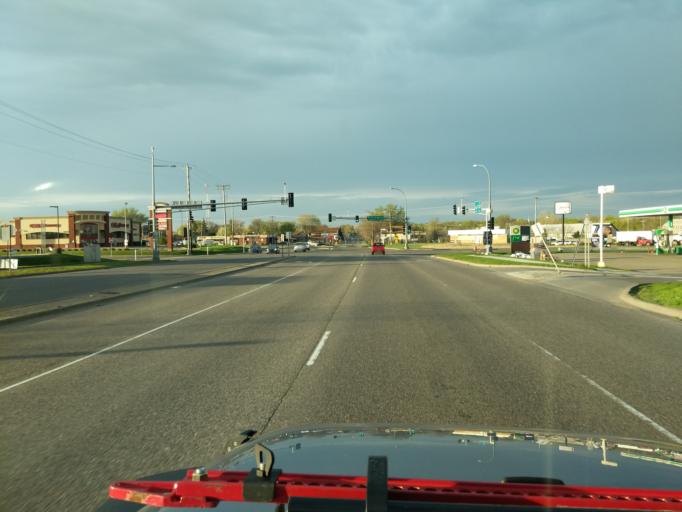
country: US
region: Minnesota
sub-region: Hennepin County
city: Rogers
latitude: 45.1931
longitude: -93.5528
